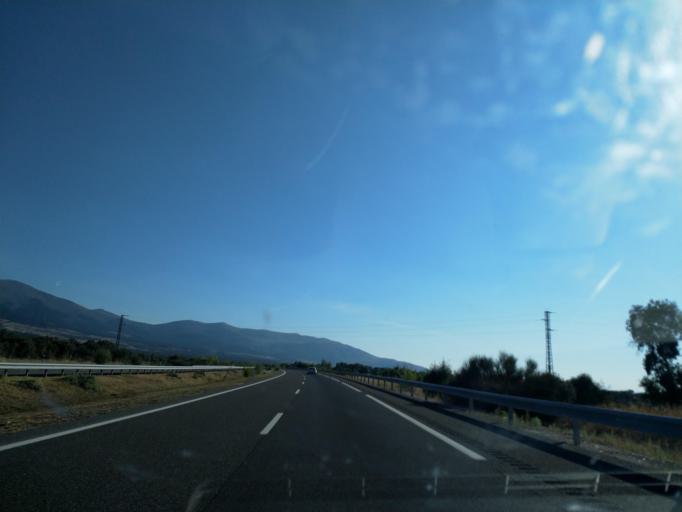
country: ES
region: Castille and Leon
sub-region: Provincia de Segovia
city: Segovia
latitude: 40.8903
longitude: -4.1152
